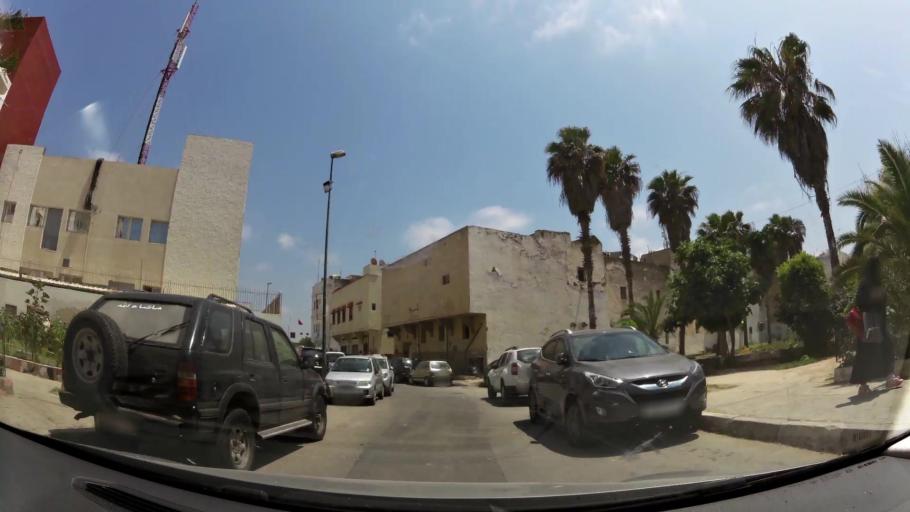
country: MA
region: Rabat-Sale-Zemmour-Zaer
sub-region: Rabat
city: Rabat
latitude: 34.0113
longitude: -6.8599
